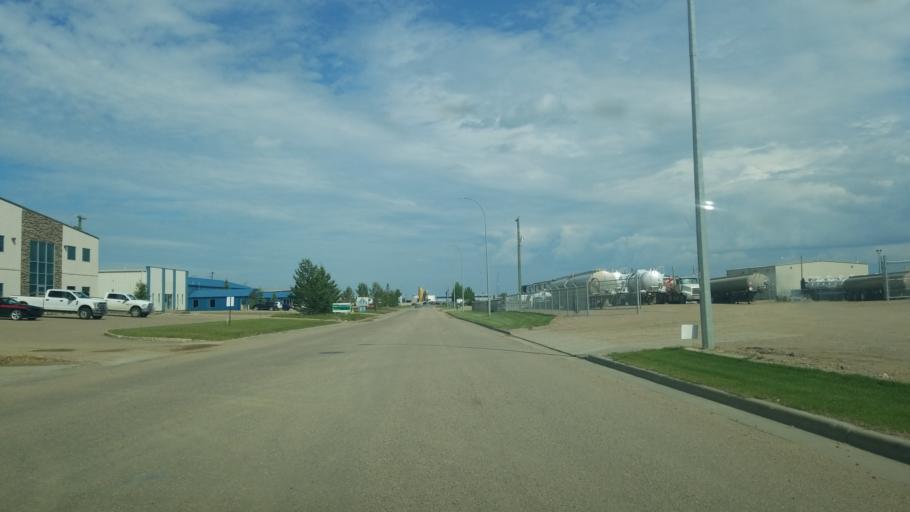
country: CA
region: Saskatchewan
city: Lloydminster
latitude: 53.2915
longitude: -110.0406
